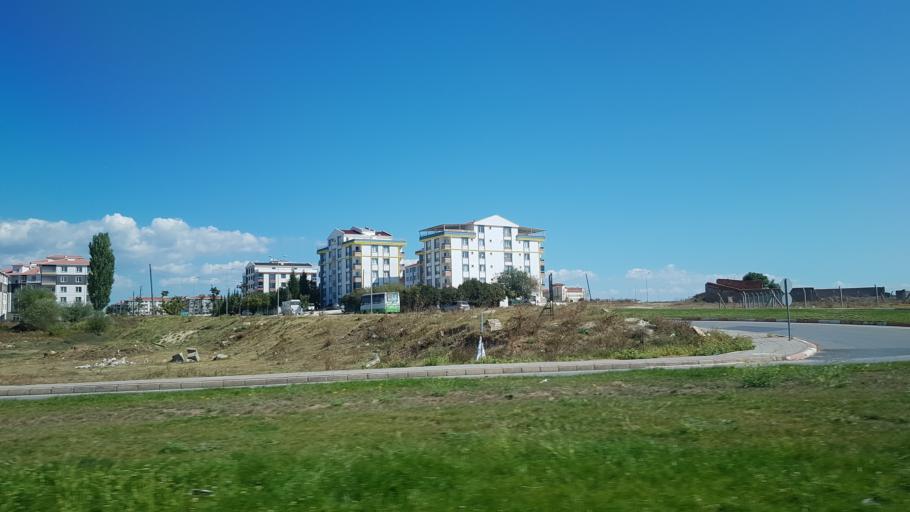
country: TR
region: Kirklareli
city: Kirklareli
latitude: 41.7512
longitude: 27.2189
